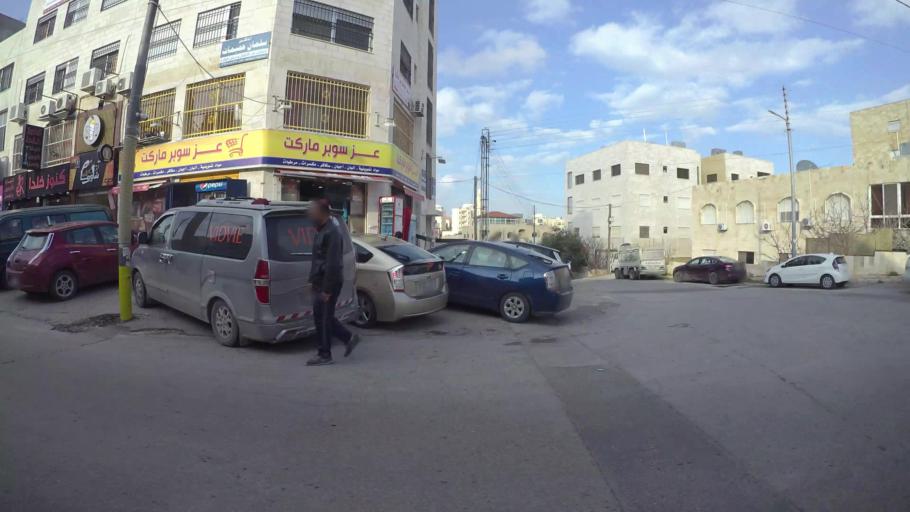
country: JO
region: Amman
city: Al Jubayhah
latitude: 31.9856
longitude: 35.8581
